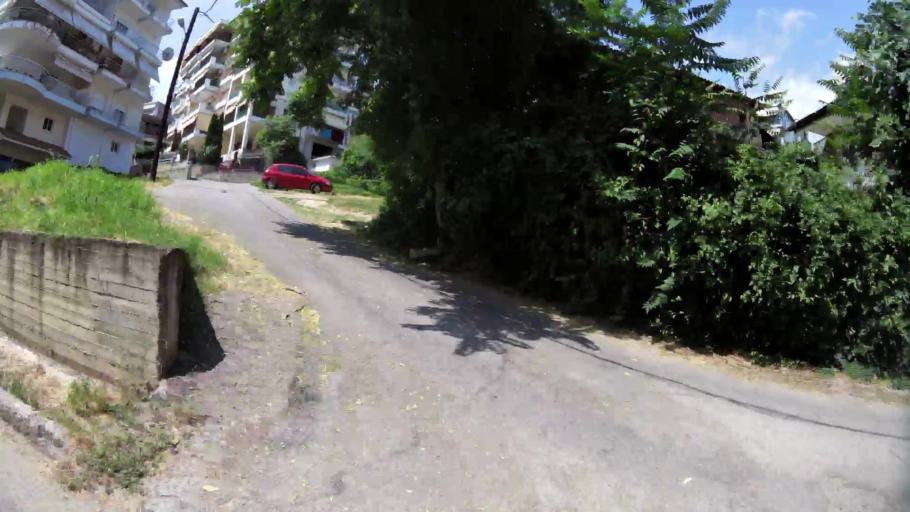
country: GR
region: Central Macedonia
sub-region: Nomos Imathias
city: Veroia
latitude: 40.5152
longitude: 22.2052
